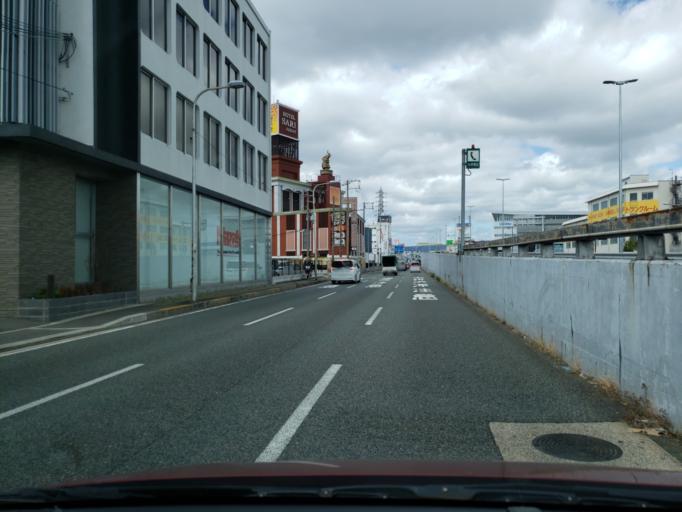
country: JP
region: Osaka
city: Toyonaka
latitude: 34.7534
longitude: 135.4627
